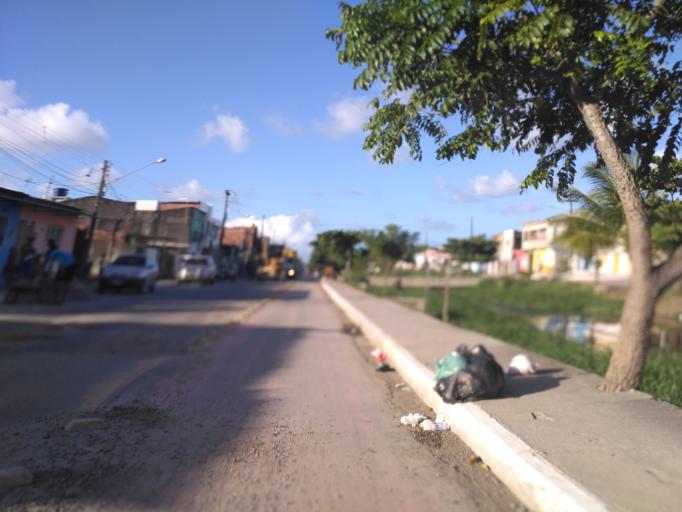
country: BR
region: Pernambuco
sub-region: Jaboatao Dos Guararapes
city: Jaboatao
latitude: -8.1837
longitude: -34.9375
